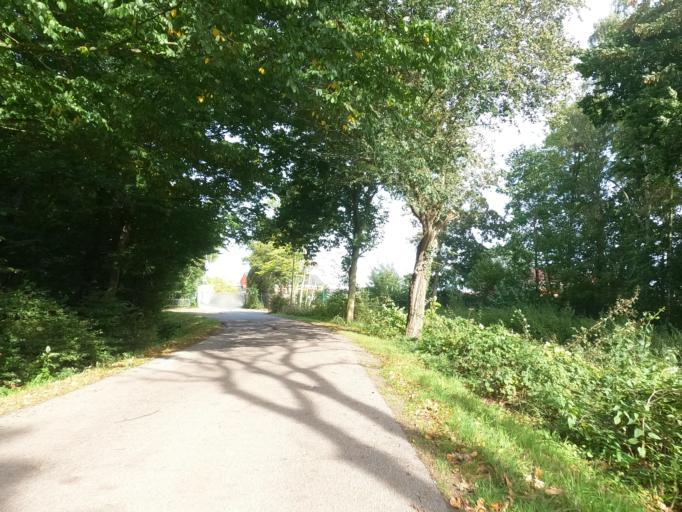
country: DE
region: Schleswig-Holstein
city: Gromitz
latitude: 54.1830
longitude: 10.9941
